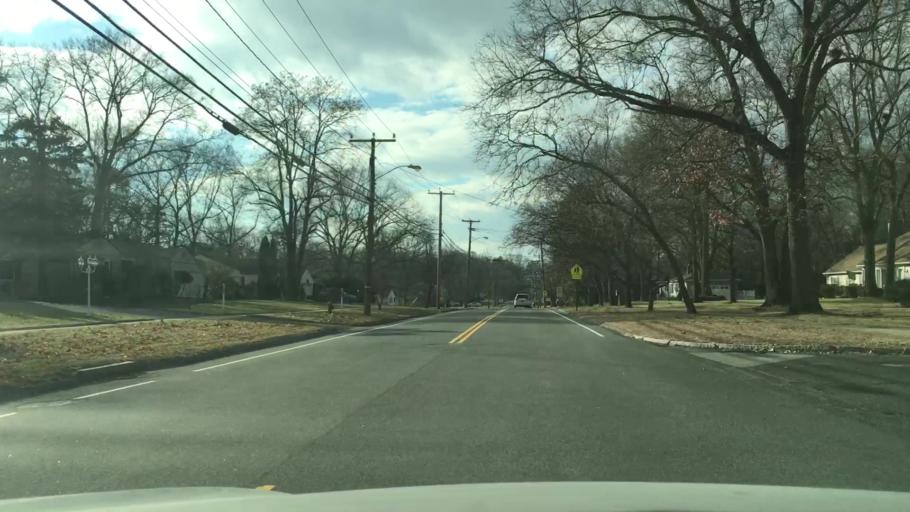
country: US
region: Connecticut
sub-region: Hartford County
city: Sherwood Manor
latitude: 42.0379
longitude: -72.5564
